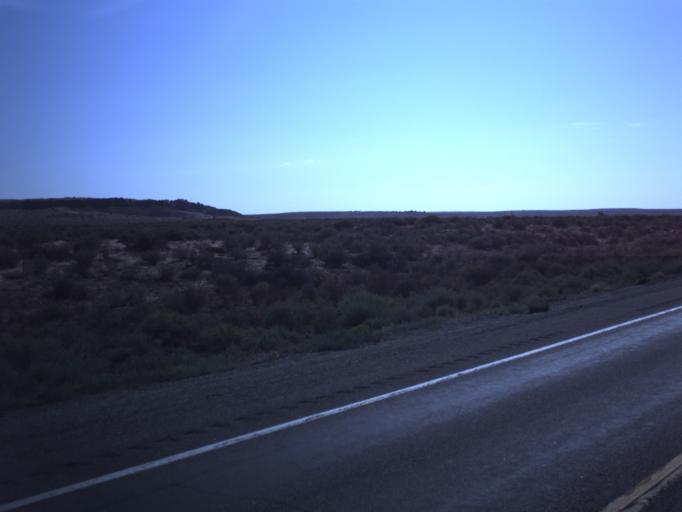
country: US
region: Utah
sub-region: San Juan County
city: Blanding
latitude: 37.1889
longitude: -109.5946
